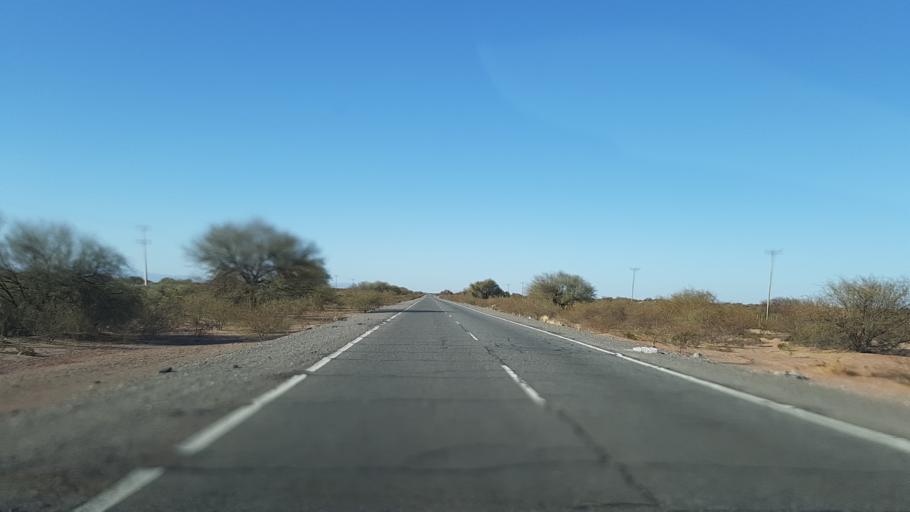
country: AR
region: San Juan
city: Caucete
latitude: -31.6078
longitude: -67.7163
